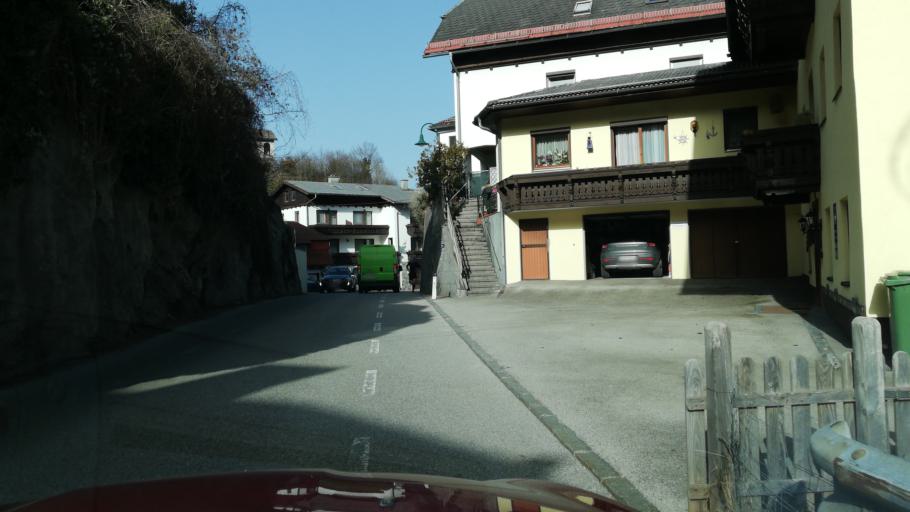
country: AT
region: Upper Austria
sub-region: Politischer Bezirk Gmunden
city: Ebensee
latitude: 47.8438
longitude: 13.7888
